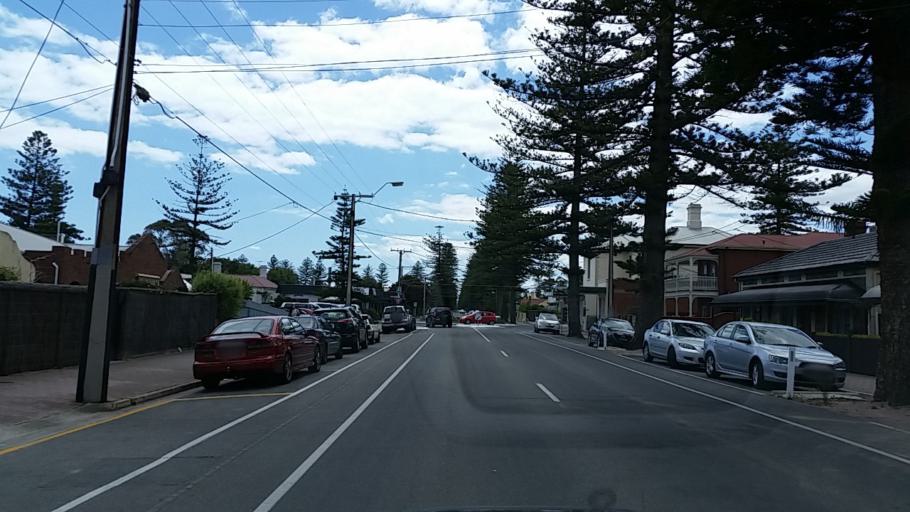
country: AU
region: South Australia
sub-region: Adelaide
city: Glenelg
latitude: -34.9889
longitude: 138.5184
